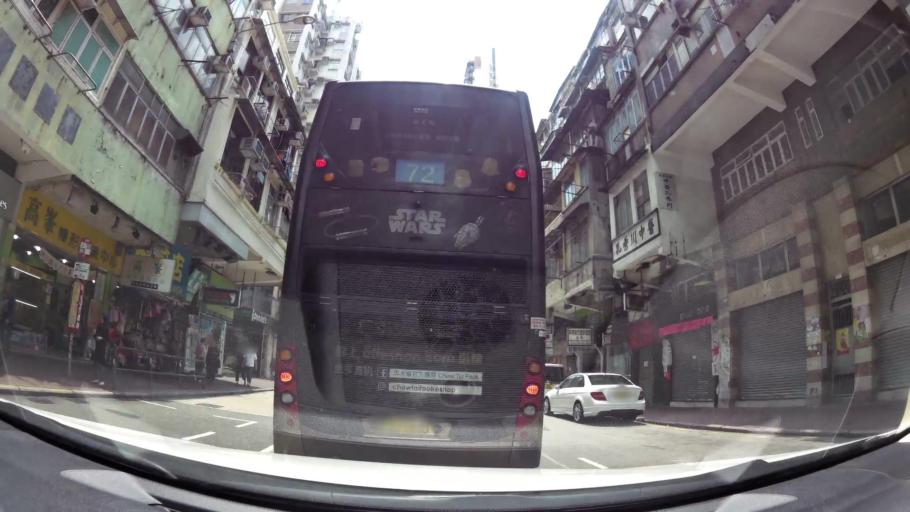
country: HK
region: Sham Shui Po
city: Sham Shui Po
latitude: 22.3369
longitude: 114.1582
